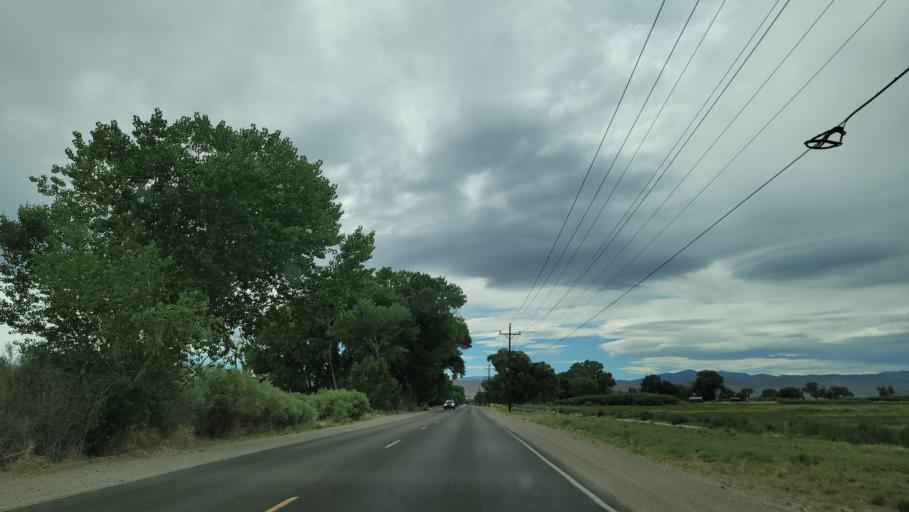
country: US
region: Nevada
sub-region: Lyon County
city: Yerington
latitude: 39.0482
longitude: -119.1515
